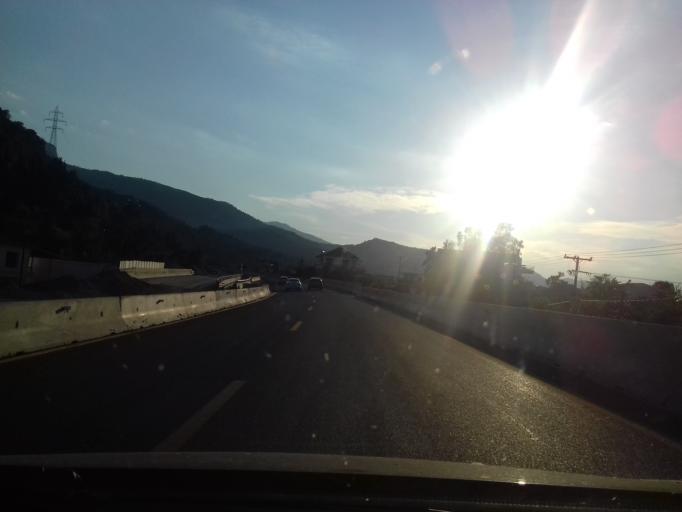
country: GR
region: West Greece
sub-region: Nomos Achaias
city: Aiyira
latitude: 38.1339
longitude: 22.4290
